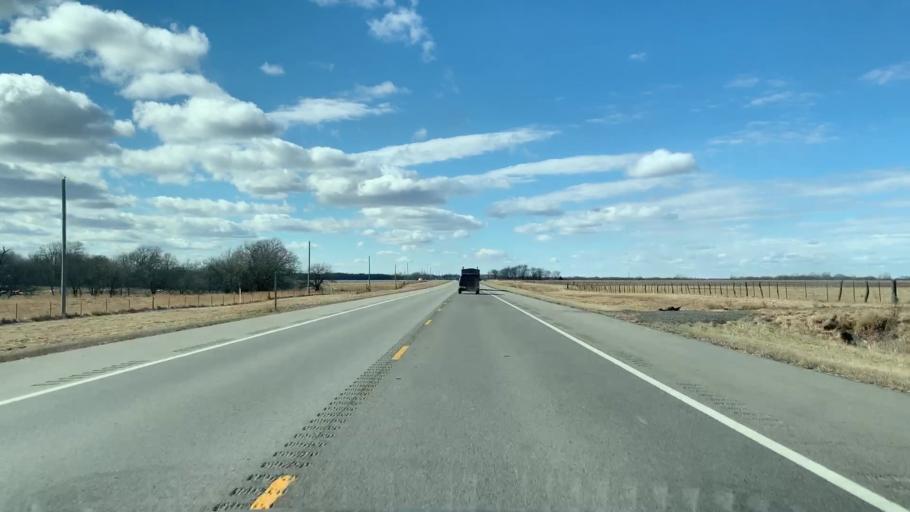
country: US
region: Kansas
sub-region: Crawford County
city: Pittsburg
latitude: 37.3397
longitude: -94.8603
